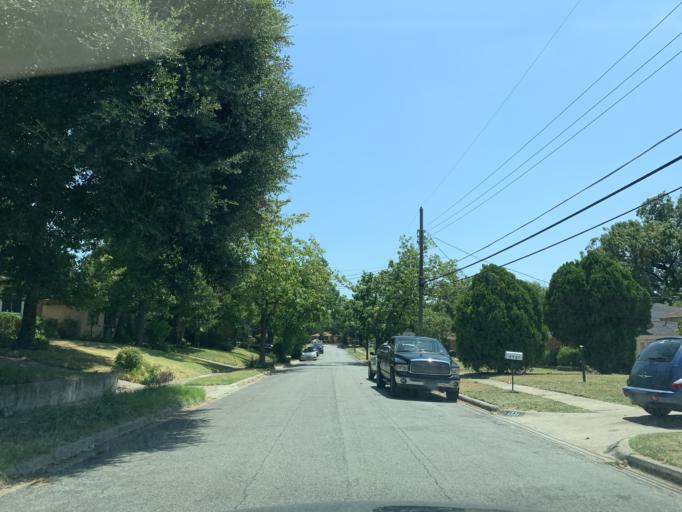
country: US
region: Texas
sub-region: Dallas County
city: Cockrell Hill
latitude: 32.6884
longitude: -96.8084
